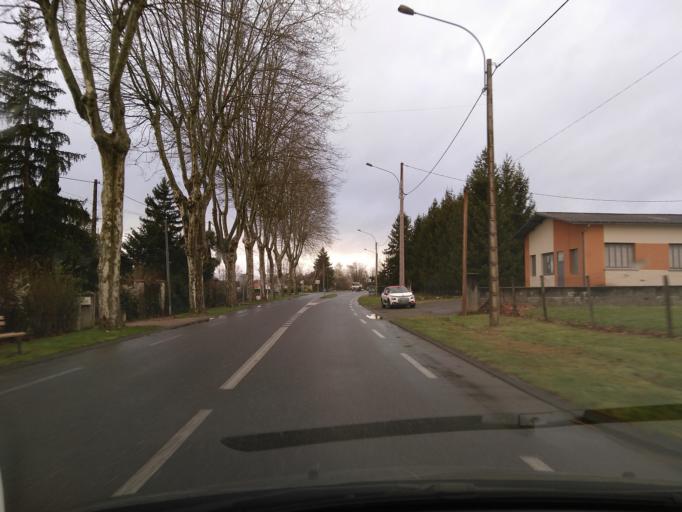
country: FR
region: Midi-Pyrenees
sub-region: Departement de la Haute-Garonne
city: Montesquieu-Volvestre
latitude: 43.2141
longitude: 1.2237
